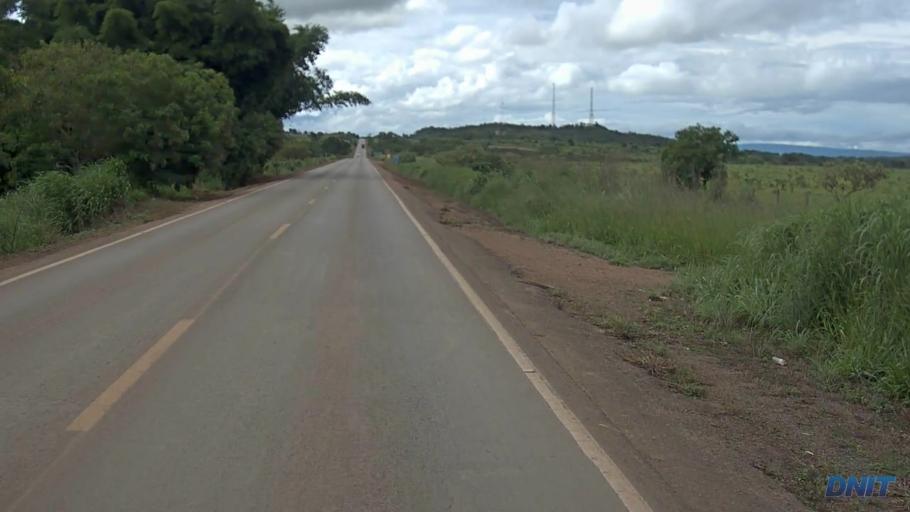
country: BR
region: Goias
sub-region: Padre Bernardo
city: Padre Bernardo
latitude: -15.2390
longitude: -48.2729
